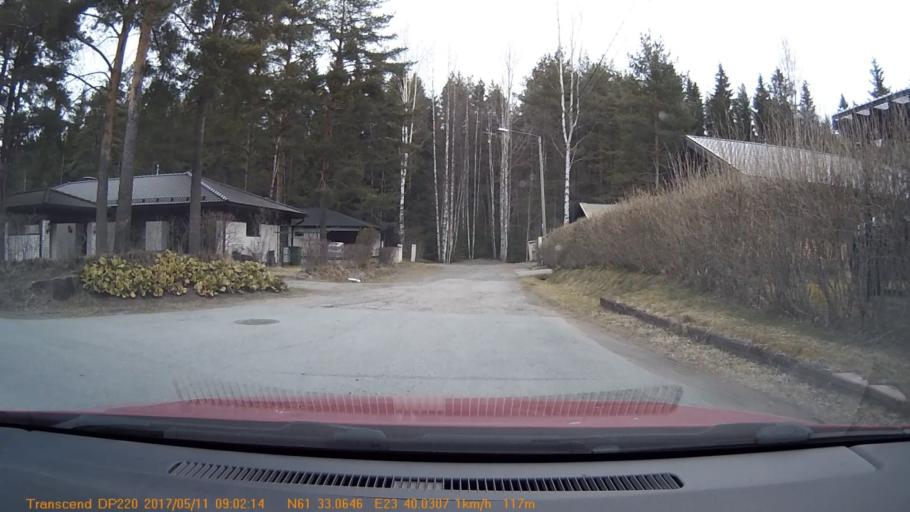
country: FI
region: Pirkanmaa
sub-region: Tampere
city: Yloejaervi
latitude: 61.5511
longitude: 23.6672
